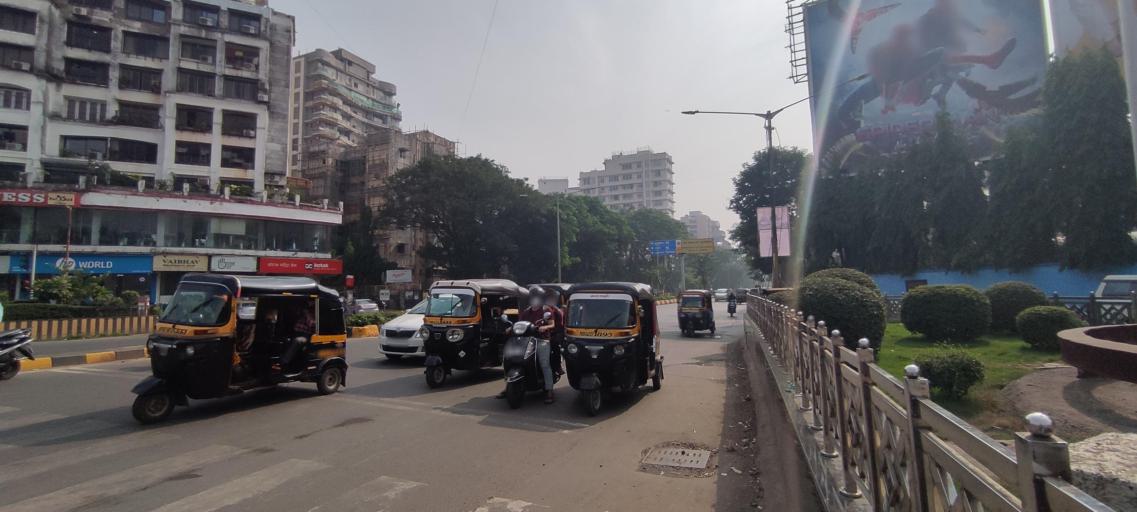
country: IN
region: Maharashtra
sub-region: Mumbai Suburban
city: Mumbai
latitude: 19.1160
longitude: 72.8298
